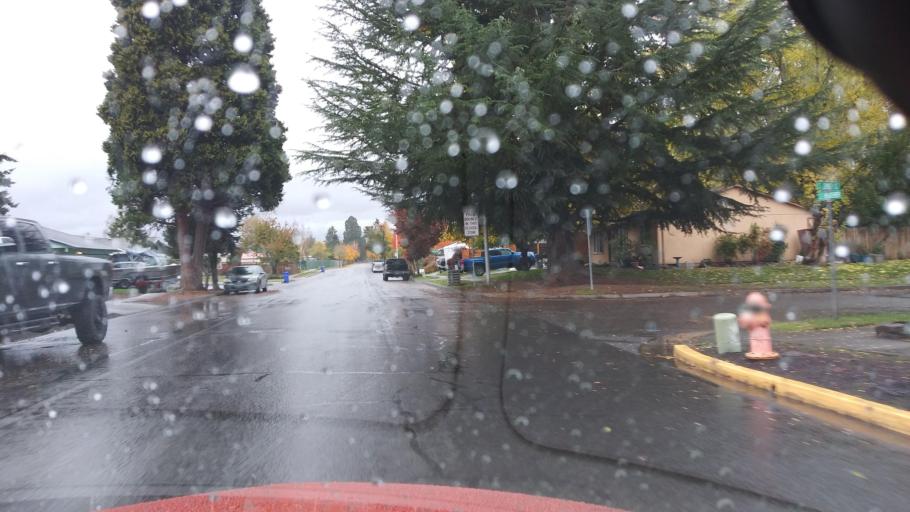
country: US
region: Oregon
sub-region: Washington County
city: Cornelius
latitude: 45.5140
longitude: -123.0689
